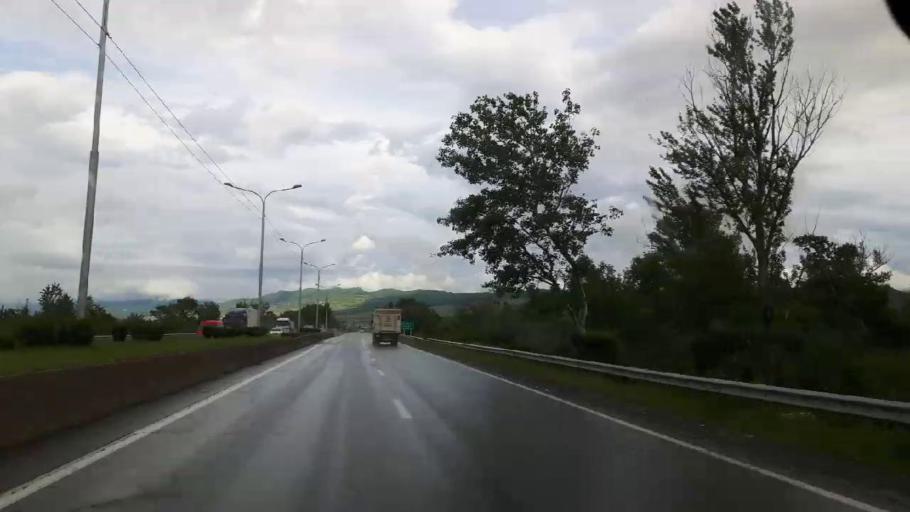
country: GE
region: Shida Kartli
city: Kaspi
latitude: 41.9095
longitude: 44.5693
